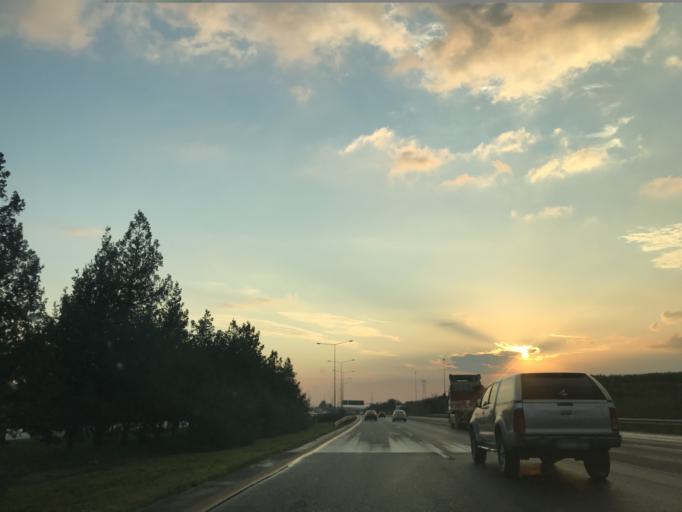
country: TR
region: Mersin
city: Yenice
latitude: 37.0340
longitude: 35.1237
